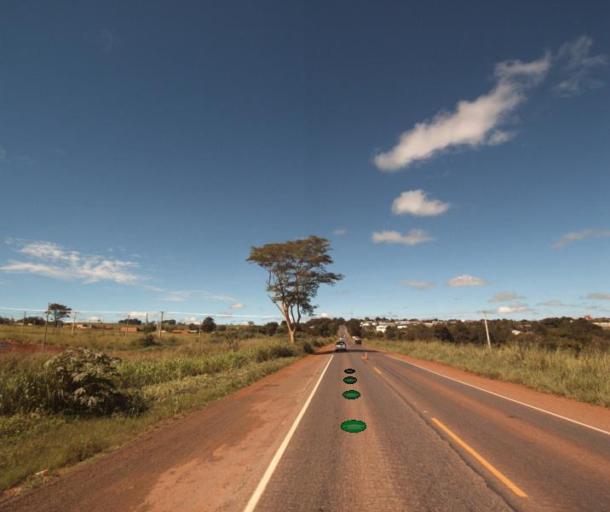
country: BR
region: Goias
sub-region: Rialma
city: Rialma
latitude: -15.3048
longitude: -49.5709
